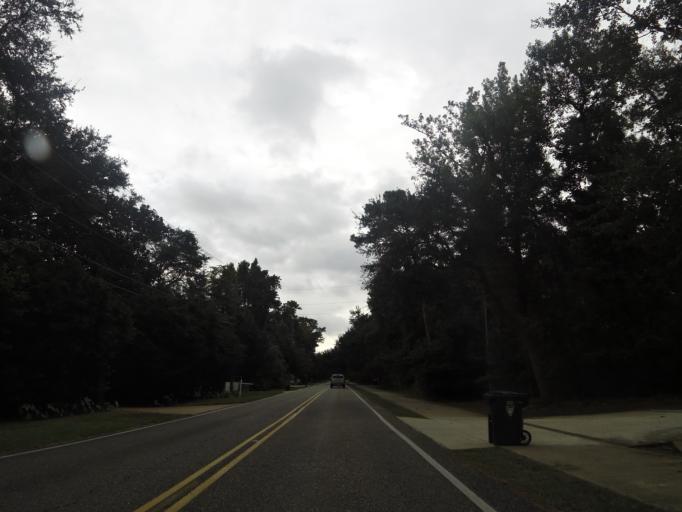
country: US
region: Alabama
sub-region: Baldwin County
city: Point Clear
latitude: 30.4638
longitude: -87.9169
